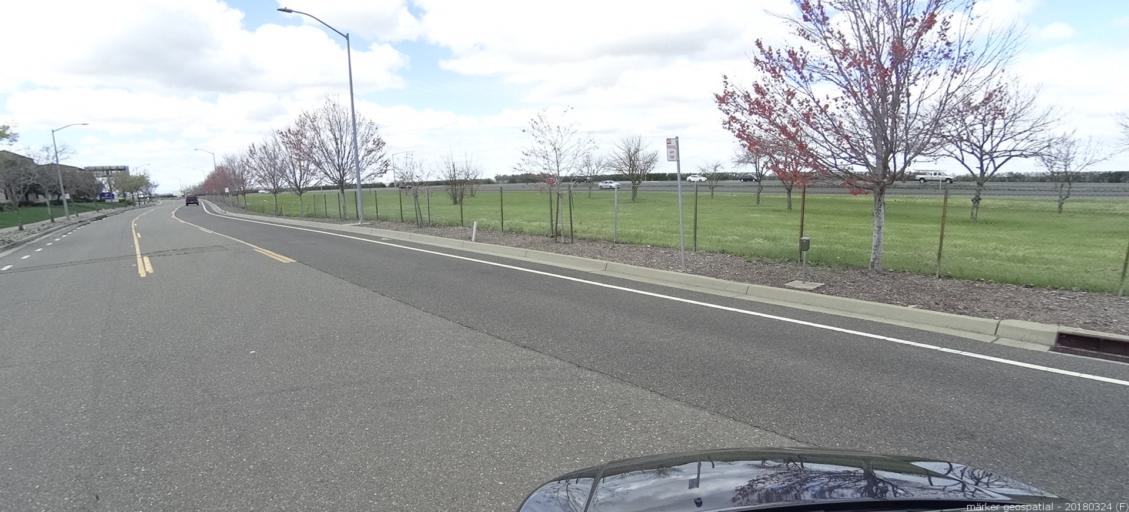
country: US
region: California
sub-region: Yolo County
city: West Sacramento
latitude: 38.6697
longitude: -121.5470
